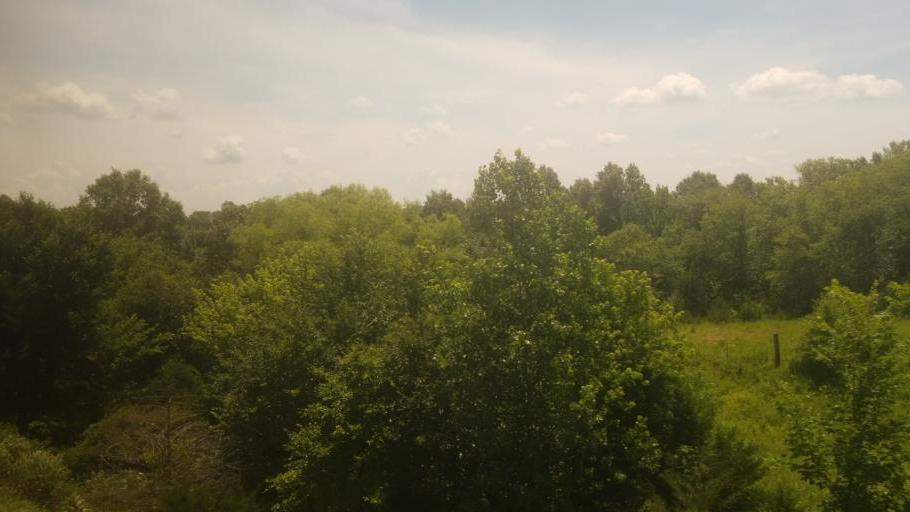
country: US
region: Missouri
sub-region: Linn County
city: Marceline
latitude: 39.8677
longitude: -92.7876
